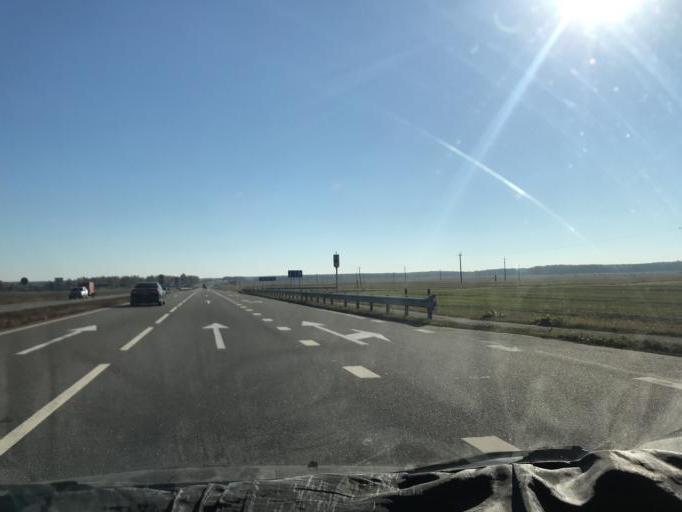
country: BY
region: Mogilev
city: Yalizava
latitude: 53.2221
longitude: 29.0178
